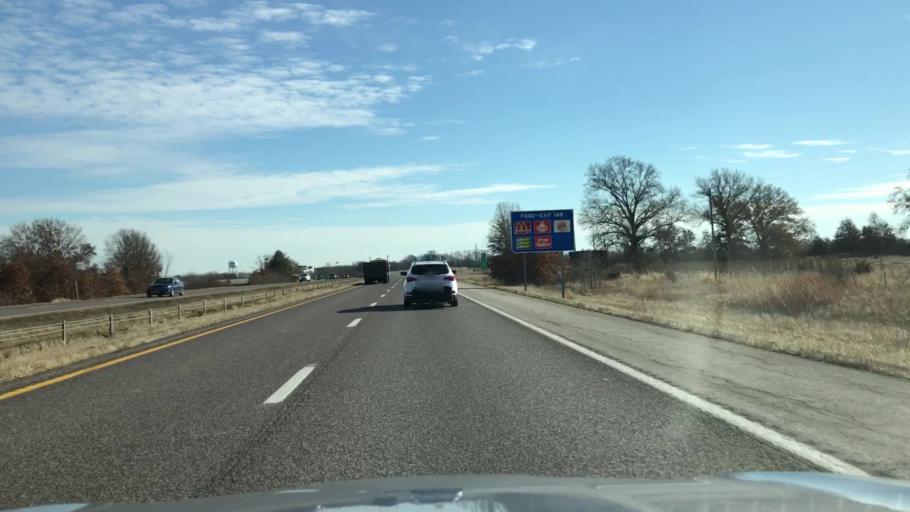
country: US
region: Missouri
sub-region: Callaway County
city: Fulton
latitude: 38.9476
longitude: -91.9570
